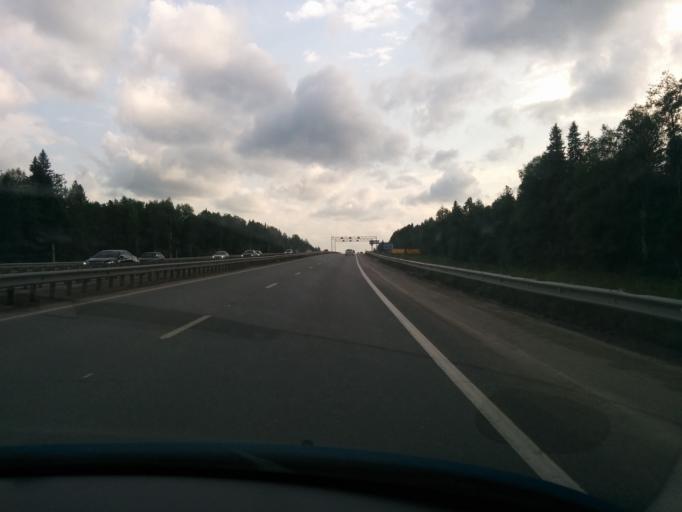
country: RU
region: Perm
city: Ferma
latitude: 58.0289
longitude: 56.4307
